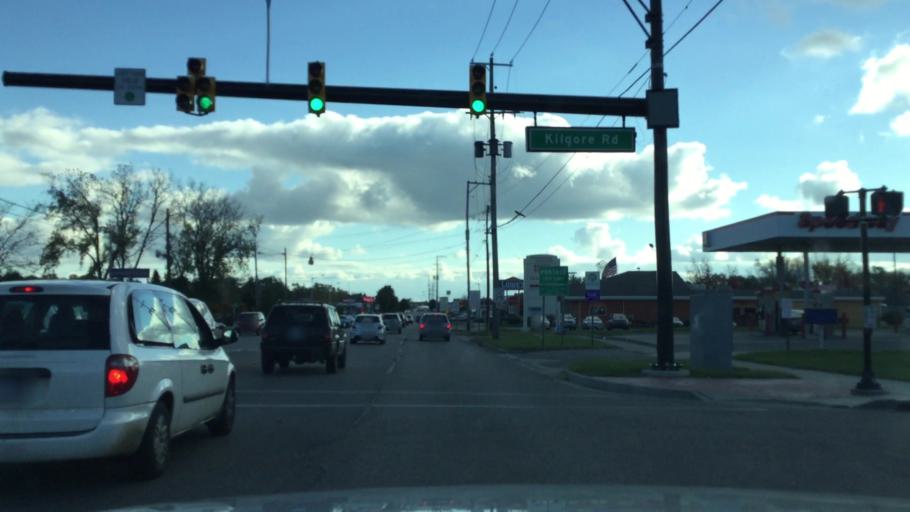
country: US
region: Michigan
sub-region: Kalamazoo County
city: Portage
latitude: 42.2451
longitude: -85.5897
